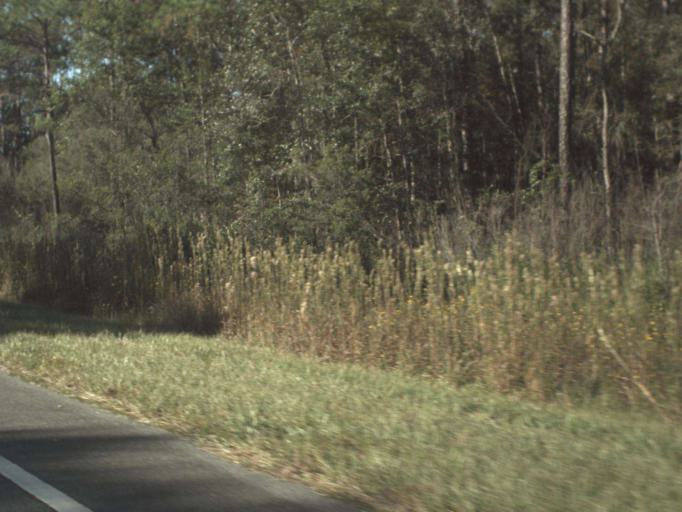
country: US
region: Florida
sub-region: Wakulla County
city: Crawfordville
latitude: 30.3192
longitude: -84.4487
